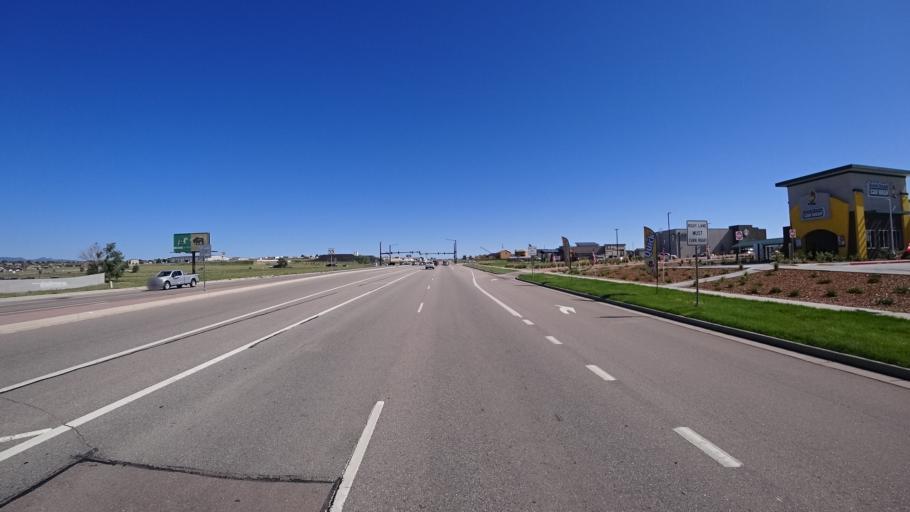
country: US
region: Colorado
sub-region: El Paso County
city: Cimarron Hills
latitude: 38.8661
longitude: -104.6826
